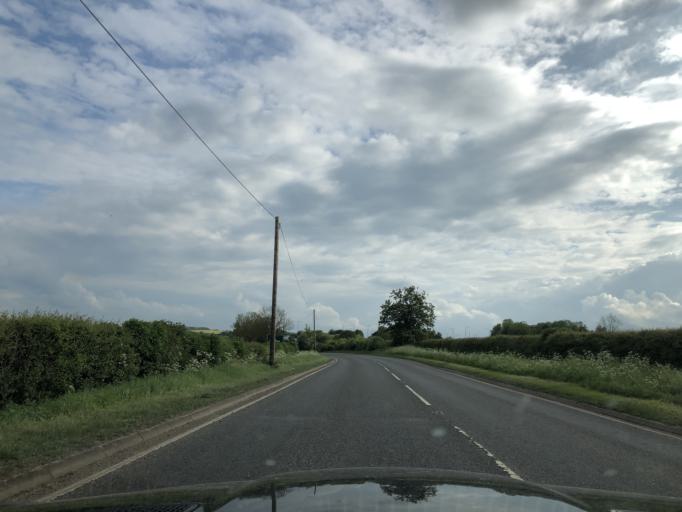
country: GB
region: England
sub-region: Warwickshire
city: Shipston on Stour
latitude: 52.0993
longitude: -1.6275
